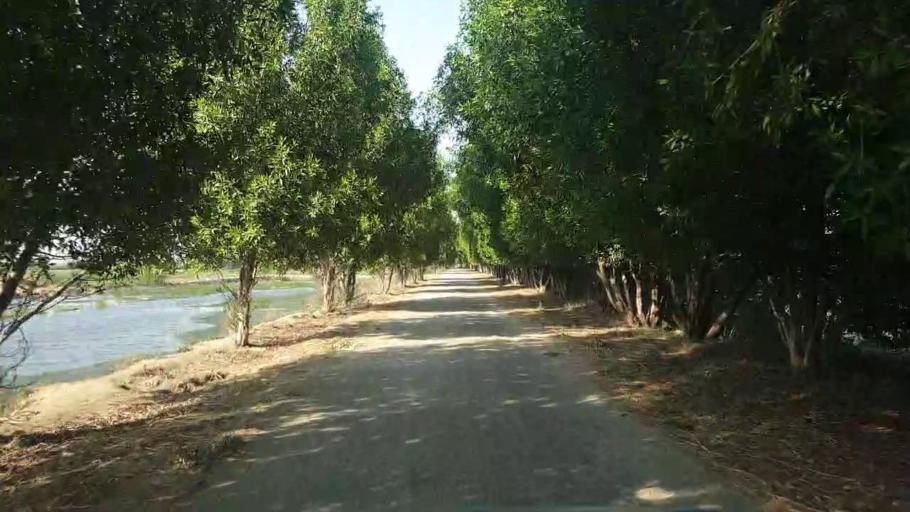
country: PK
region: Sindh
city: Badin
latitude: 24.6236
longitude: 68.8148
